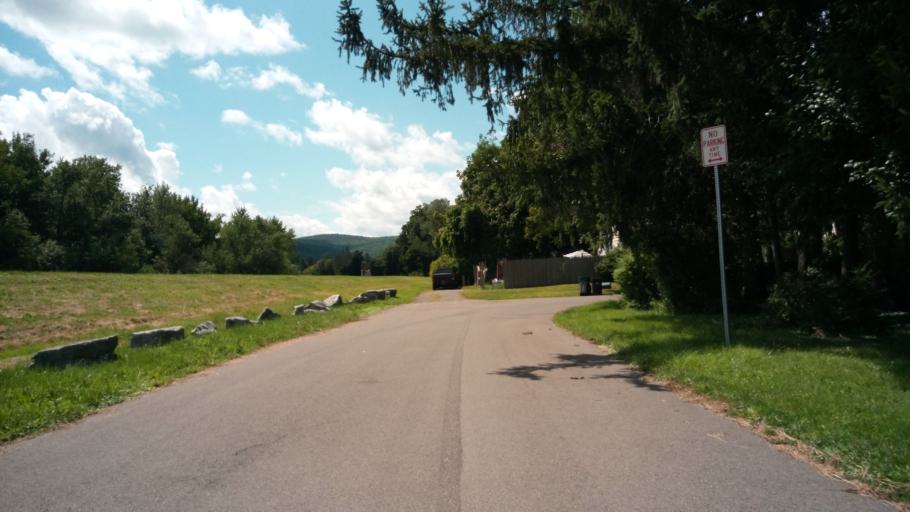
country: US
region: New York
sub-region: Chemung County
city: West Elmira
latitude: 42.0804
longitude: -76.8262
